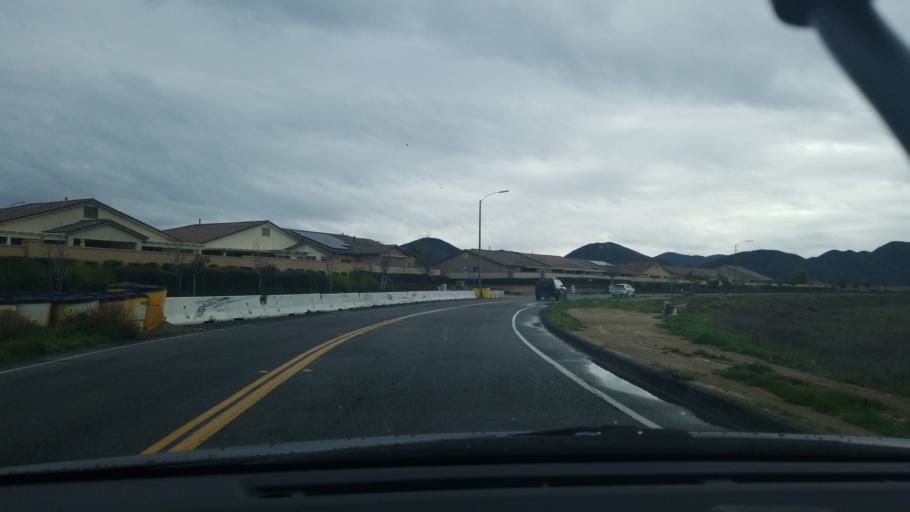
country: US
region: California
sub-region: Riverside County
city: Green Acres
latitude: 33.7235
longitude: -117.0322
